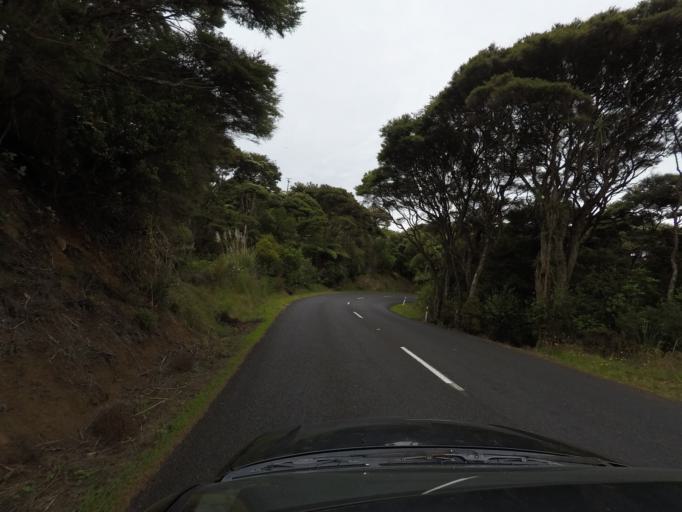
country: NZ
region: Waikato
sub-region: Waikato District
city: Raglan
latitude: -37.8251
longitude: 174.8149
